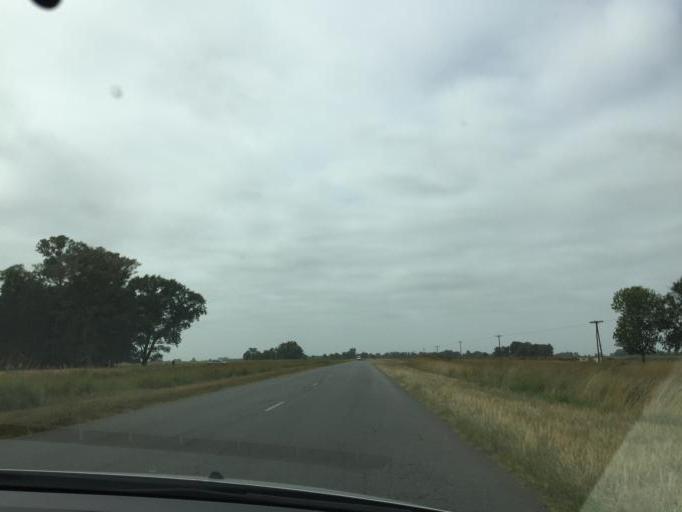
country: AR
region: Buenos Aires
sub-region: Partido de Las Flores
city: Las Flores
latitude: -36.1792
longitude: -59.0611
